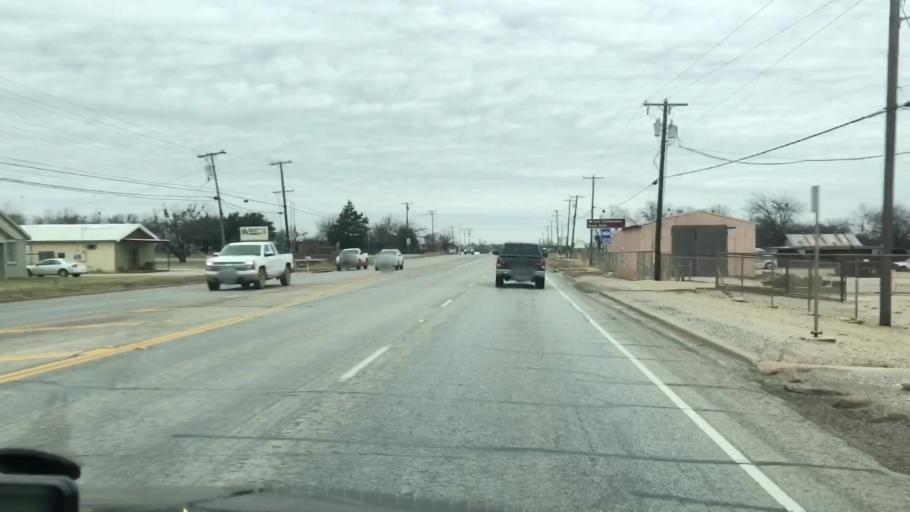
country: US
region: Texas
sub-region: Jack County
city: Jacksboro
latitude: 33.2065
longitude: -98.1543
